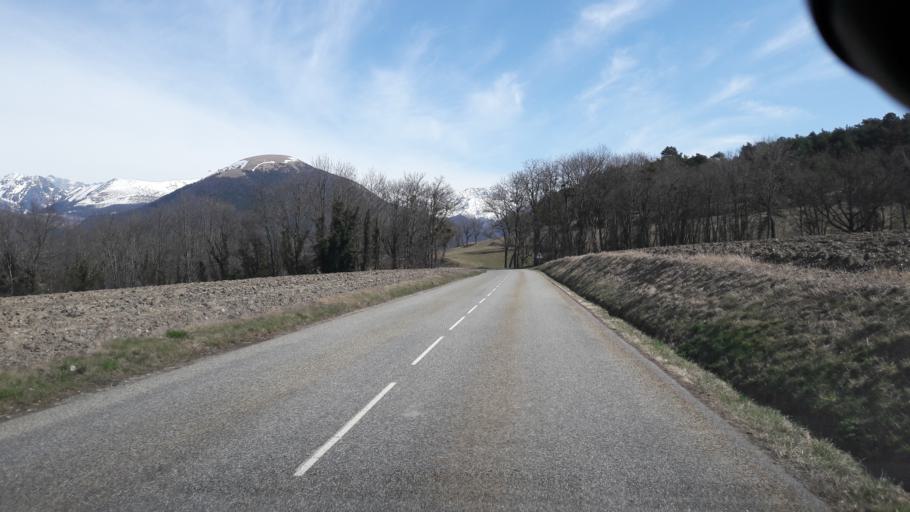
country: FR
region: Rhone-Alpes
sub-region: Departement de l'Isere
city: La Mure
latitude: 44.8439
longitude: 5.8146
